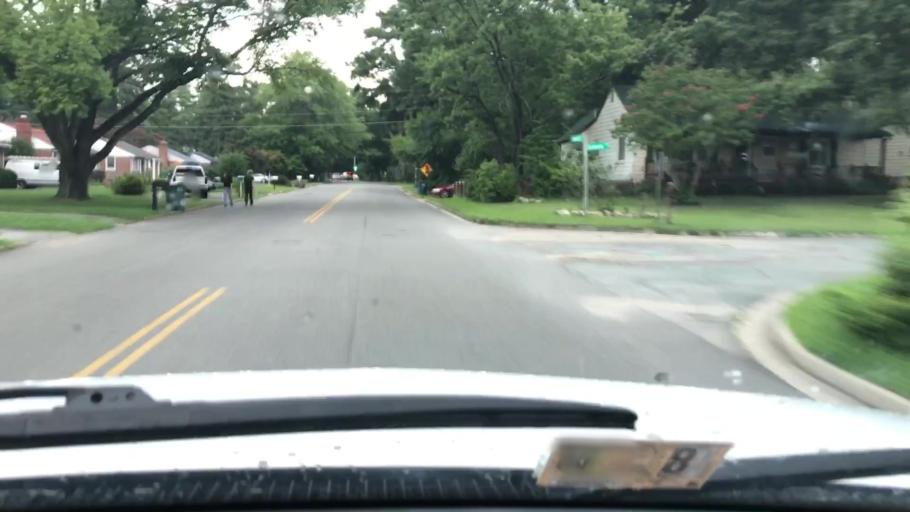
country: US
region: Virginia
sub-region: Henrico County
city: Dumbarton
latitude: 37.5989
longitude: -77.5085
